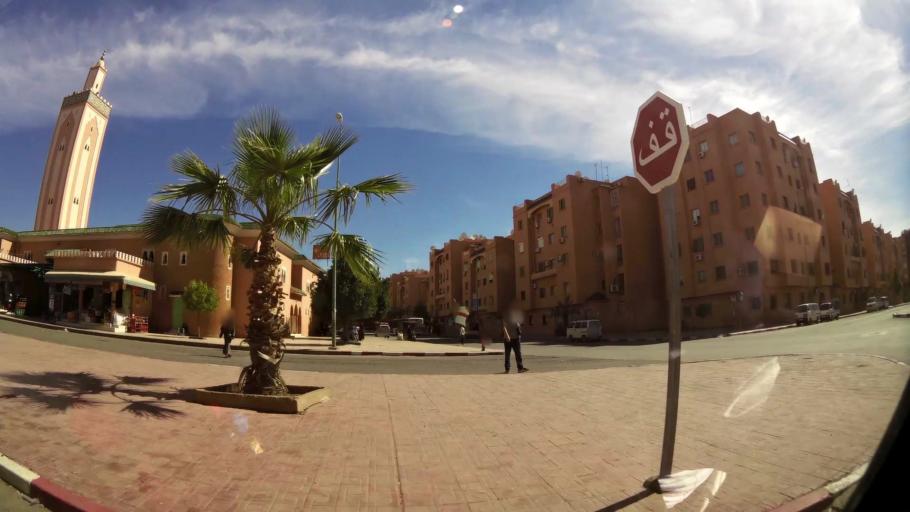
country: MA
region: Marrakech-Tensift-Al Haouz
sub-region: Marrakech
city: Marrakesh
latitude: 31.6761
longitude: -8.0174
